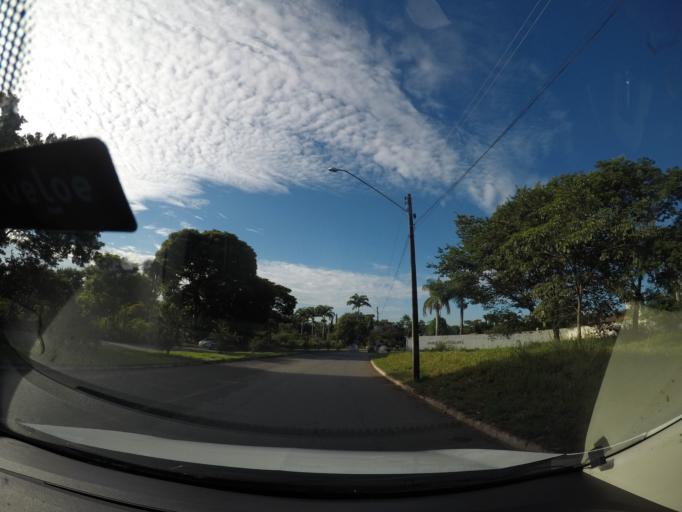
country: BR
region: Goias
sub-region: Goiania
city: Goiania
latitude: -16.7452
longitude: -49.2695
